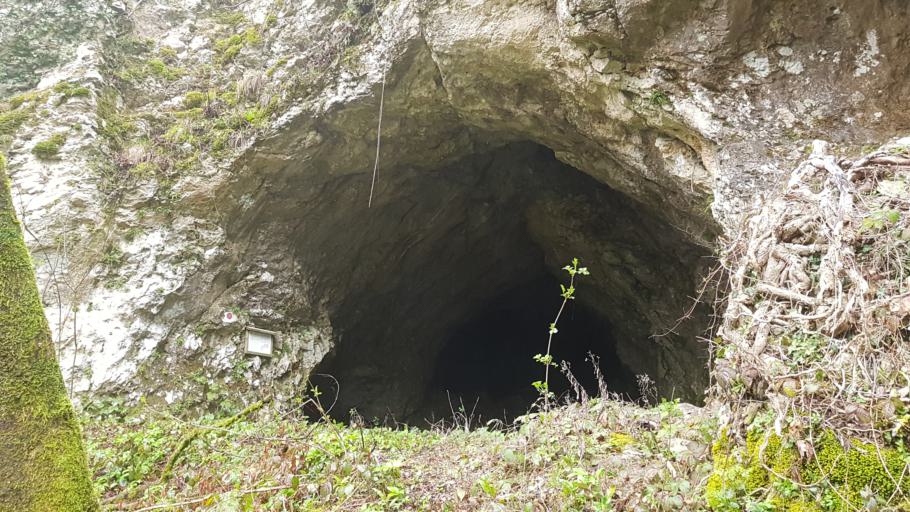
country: IT
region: Friuli Venezia Giulia
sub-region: Provincia di Udine
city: Pulfero
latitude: 46.1856
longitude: 13.4743
